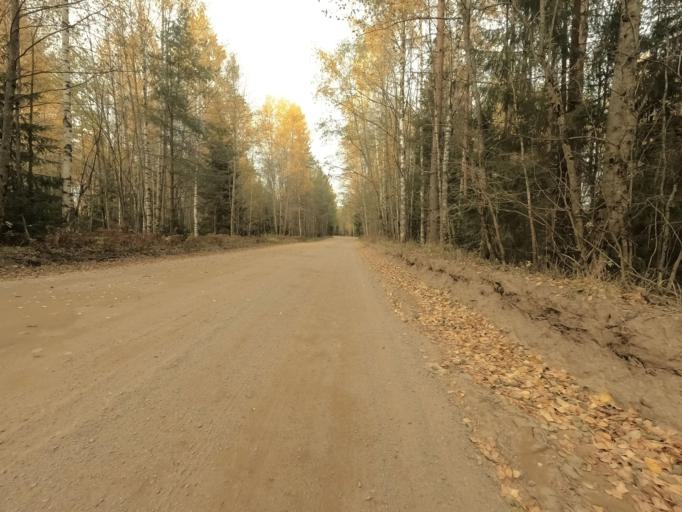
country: RU
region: Leningrad
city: Priladozhskiy
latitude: 59.6854
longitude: 31.3620
